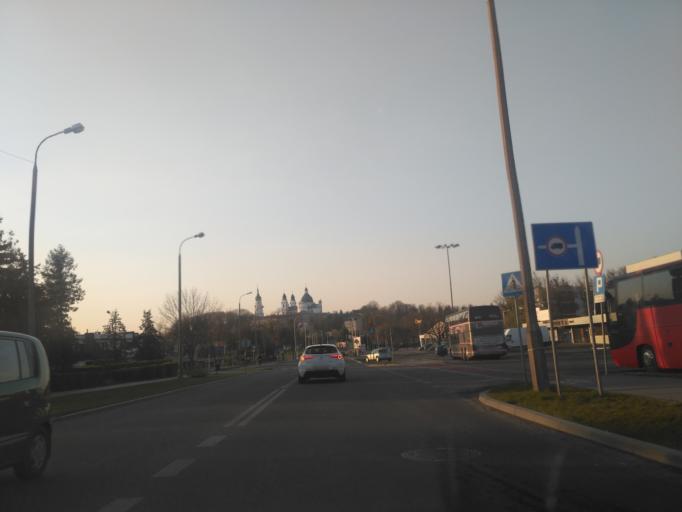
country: PL
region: Lublin Voivodeship
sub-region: Chelm
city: Chelm
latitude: 51.1255
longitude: 23.4826
